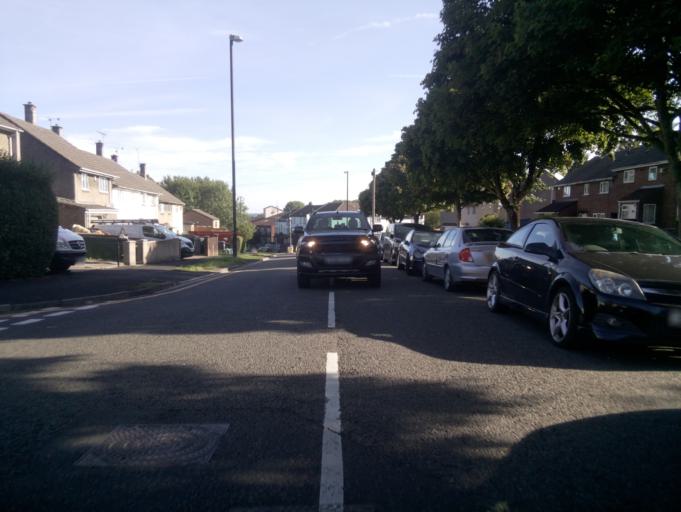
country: GB
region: England
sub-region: Bath and North East Somerset
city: Whitchurch
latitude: 51.4131
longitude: -2.5536
